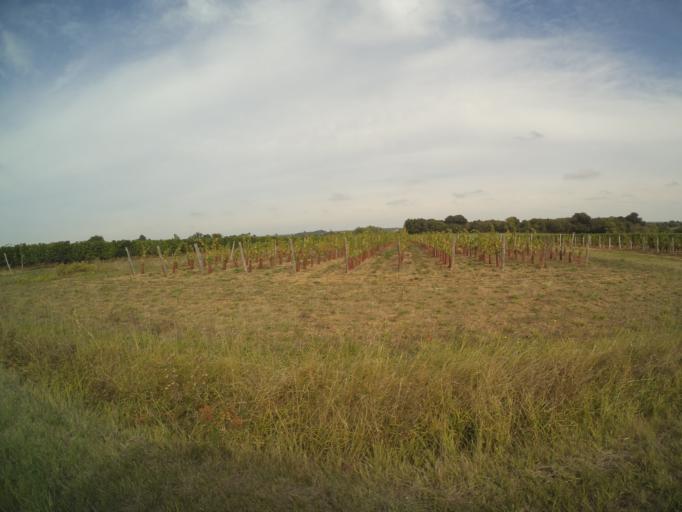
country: FR
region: Pays de la Loire
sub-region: Departement de Maine-et-Loire
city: Martigne-Briand
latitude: 47.2060
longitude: -0.4579
